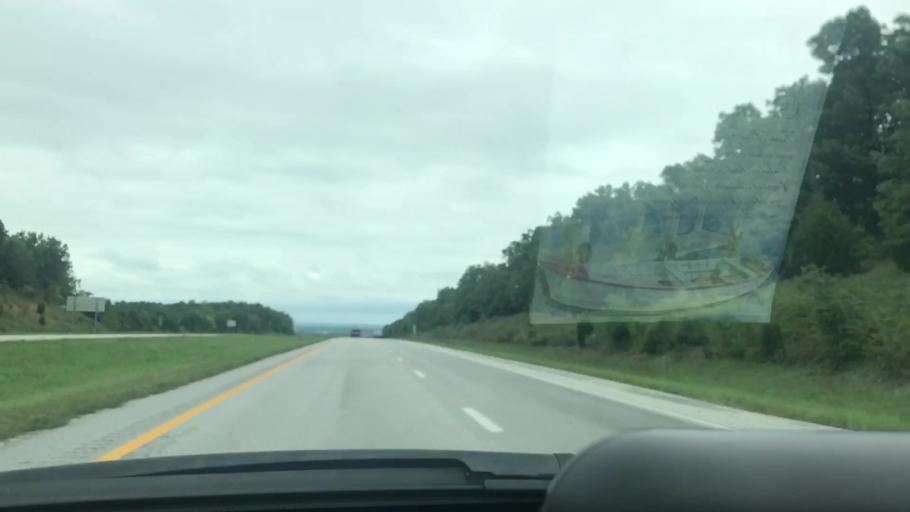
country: US
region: Missouri
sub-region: Greene County
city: Fair Grove
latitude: 37.3301
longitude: -93.1680
